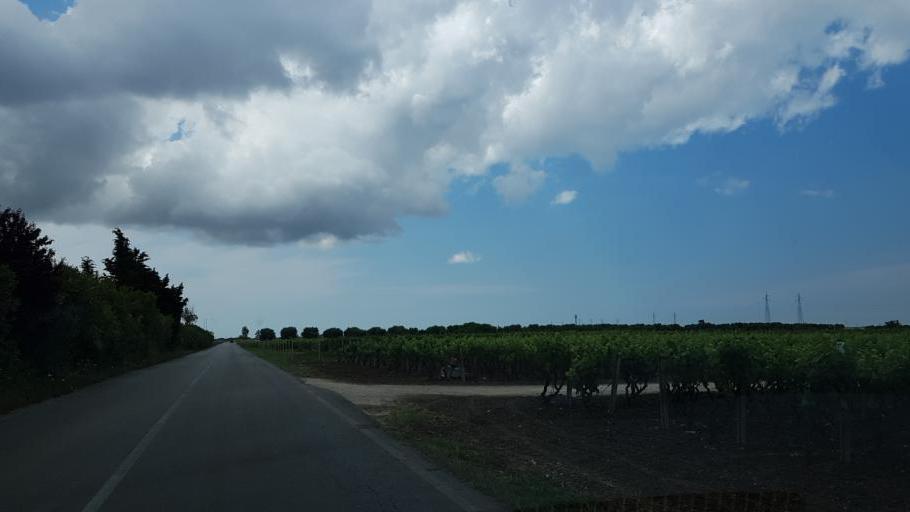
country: IT
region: Apulia
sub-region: Provincia di Brindisi
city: San Pancrazio Salentino
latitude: 40.3874
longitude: 17.8358
